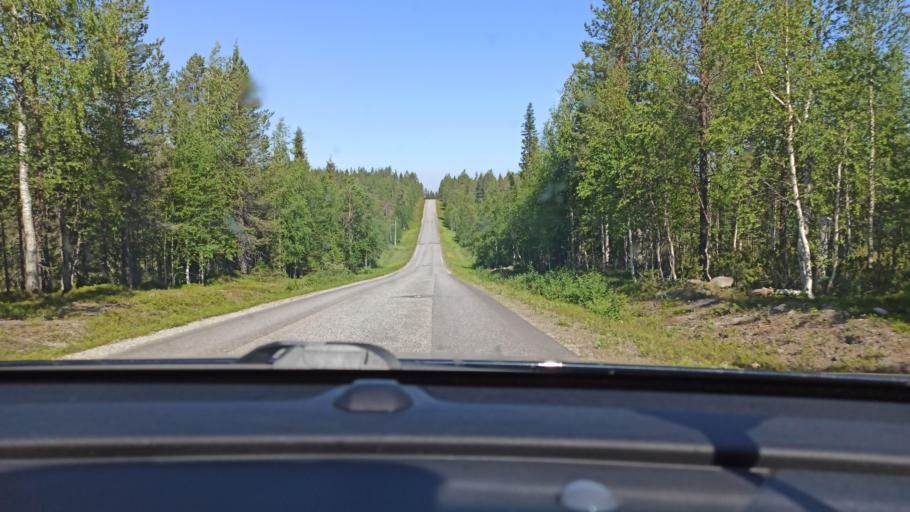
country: FI
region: Lapland
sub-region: Tunturi-Lappi
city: Kolari
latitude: 67.6766
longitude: 24.1431
